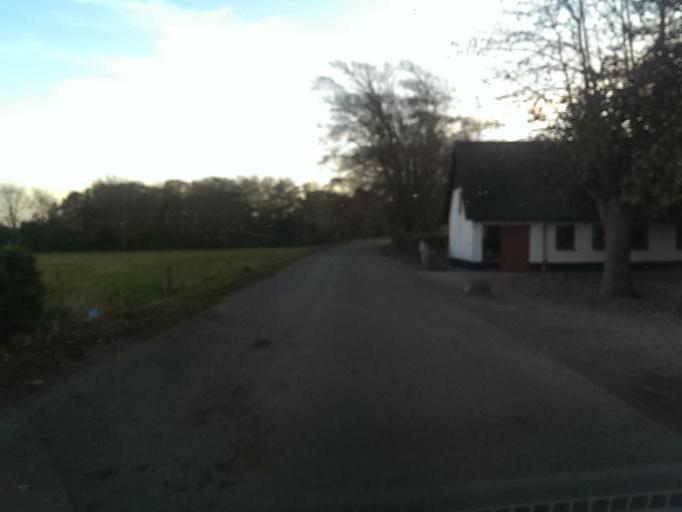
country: DK
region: South Denmark
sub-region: Esbjerg Kommune
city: Tjaereborg
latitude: 55.4739
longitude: 8.6159
